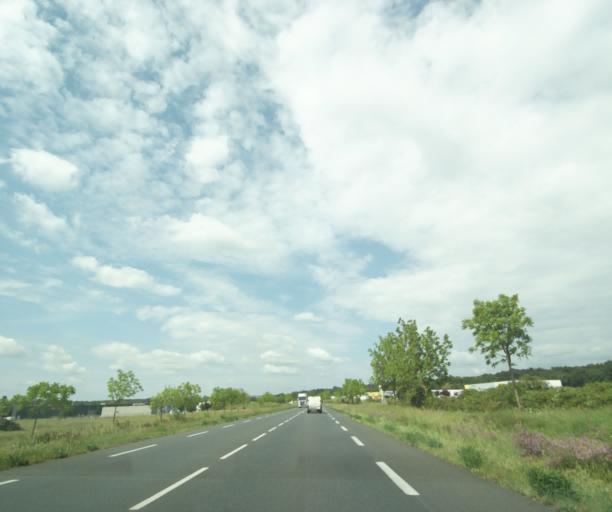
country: FR
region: Pays de la Loire
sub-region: Departement de Maine-et-Loire
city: Distre
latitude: 47.2302
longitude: -0.1137
